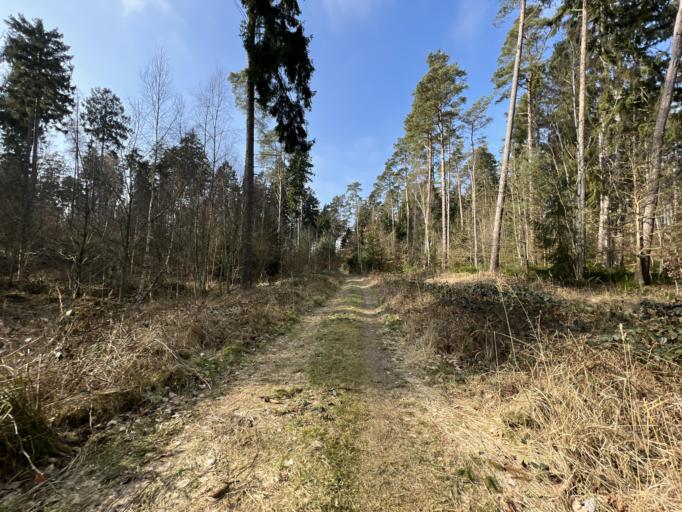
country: DE
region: Mecklenburg-Vorpommern
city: Sagard
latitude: 54.4788
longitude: 13.5589
